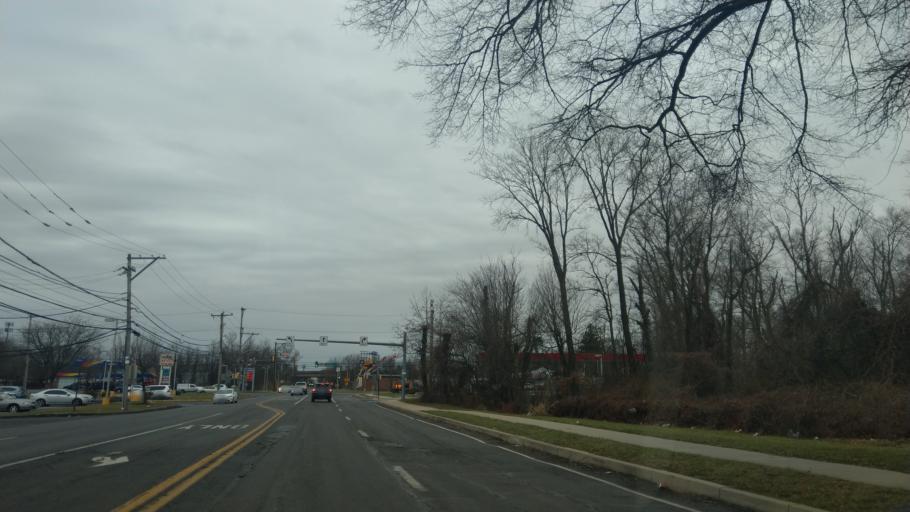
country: US
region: Pennsylvania
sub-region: Bucks County
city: Hulmeville
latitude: 40.1328
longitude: -74.8869
